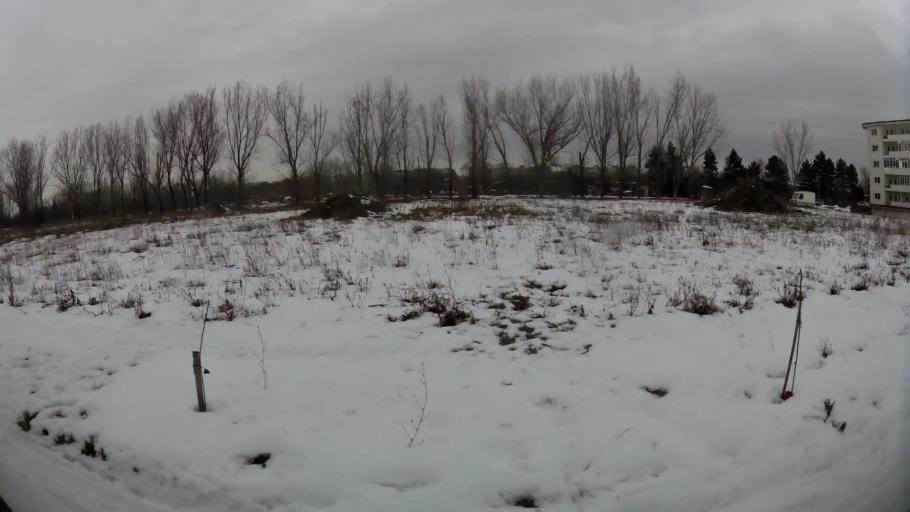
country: RO
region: Bucuresti
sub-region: Municipiul Bucuresti
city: Bucuresti
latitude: 44.4105
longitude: 26.0504
